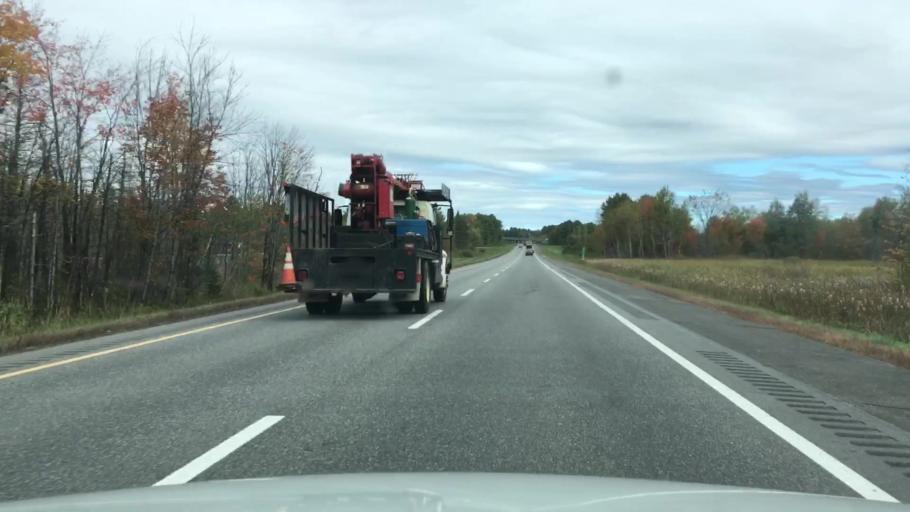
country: US
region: Maine
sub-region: Kennebec County
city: Sidney
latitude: 44.4456
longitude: -69.7217
